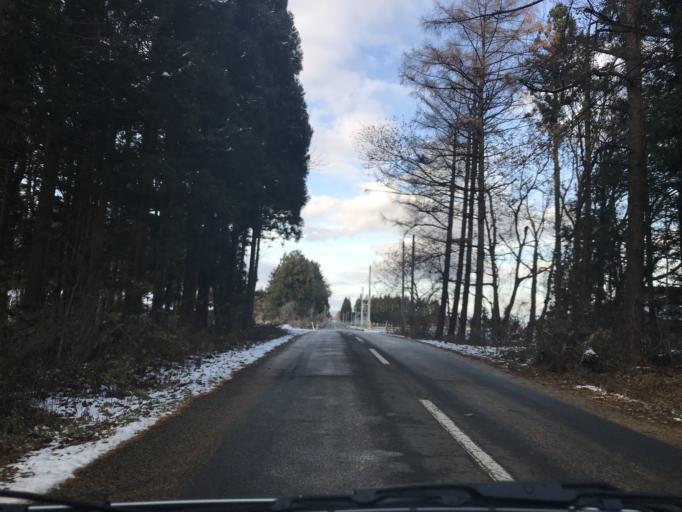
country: JP
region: Iwate
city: Kitakami
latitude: 39.2436
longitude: 141.0327
